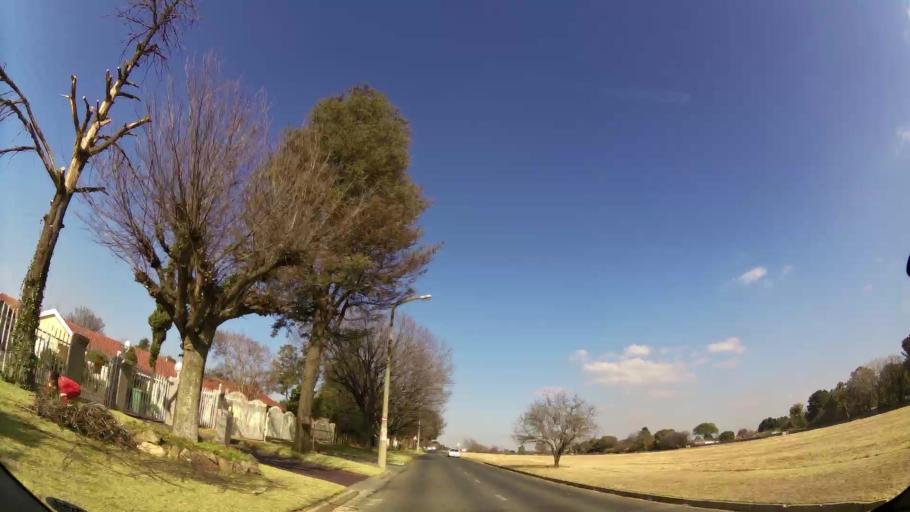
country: ZA
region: Gauteng
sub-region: Ekurhuleni Metropolitan Municipality
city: Benoni
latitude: -26.1431
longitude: 28.3358
